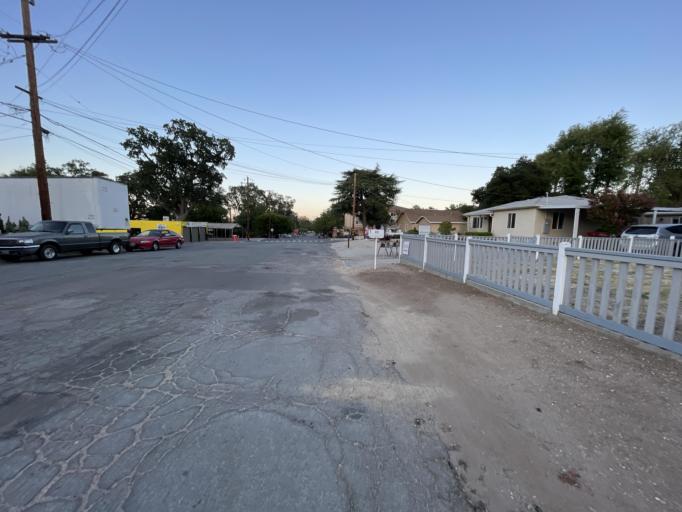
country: US
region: California
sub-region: San Luis Obispo County
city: Paso Robles
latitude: 35.6454
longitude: -120.6938
